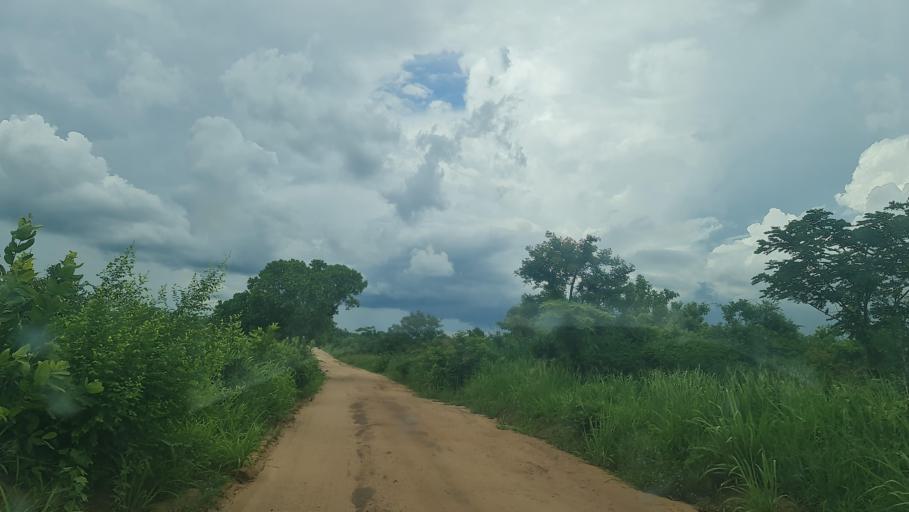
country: MW
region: Southern Region
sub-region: Nsanje District
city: Nsanje
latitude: -17.5725
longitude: 35.6539
